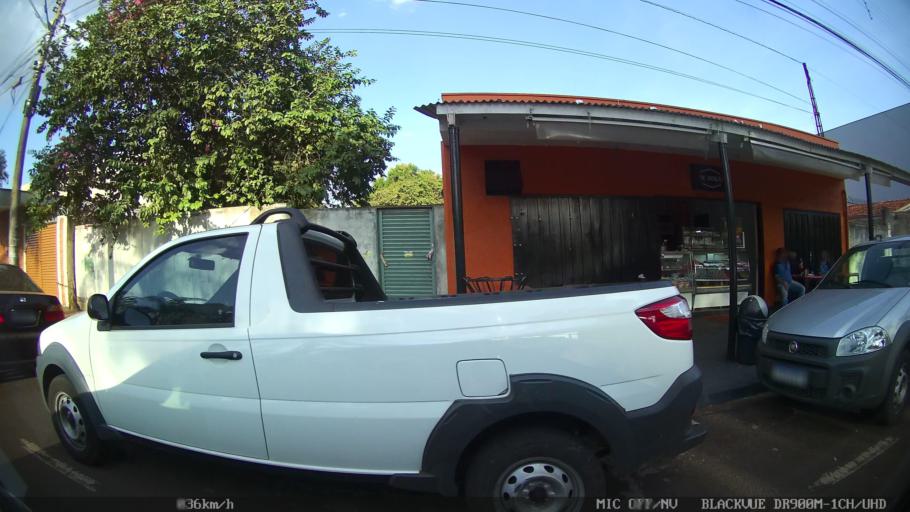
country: BR
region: Sao Paulo
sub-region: Ribeirao Preto
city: Ribeirao Preto
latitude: -21.1673
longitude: -47.8301
